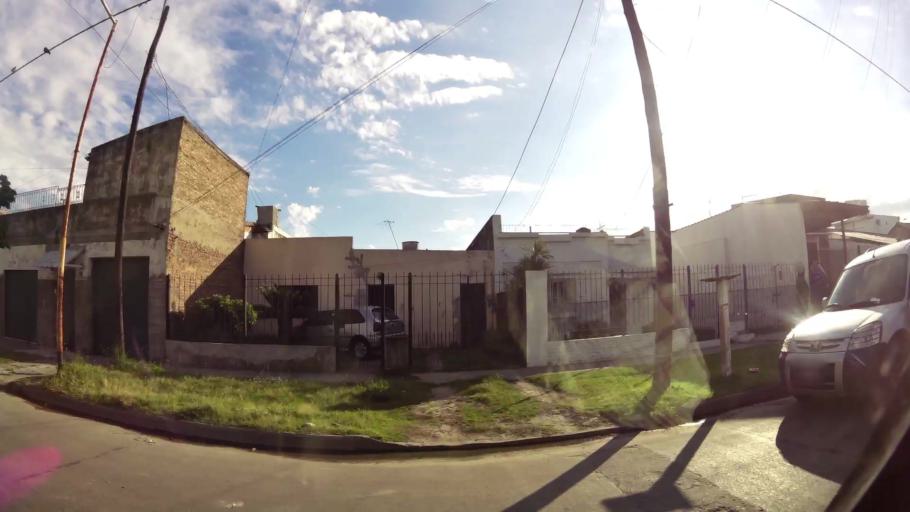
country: AR
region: Buenos Aires
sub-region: Partido de Avellaneda
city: Avellaneda
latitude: -34.6981
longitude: -58.3522
